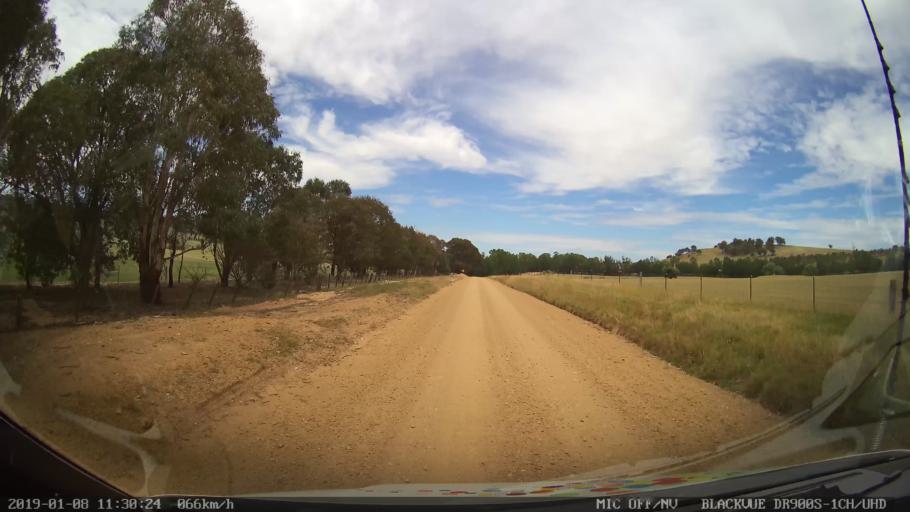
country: AU
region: New South Wales
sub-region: Guyra
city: Guyra
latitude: -30.3077
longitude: 151.5445
